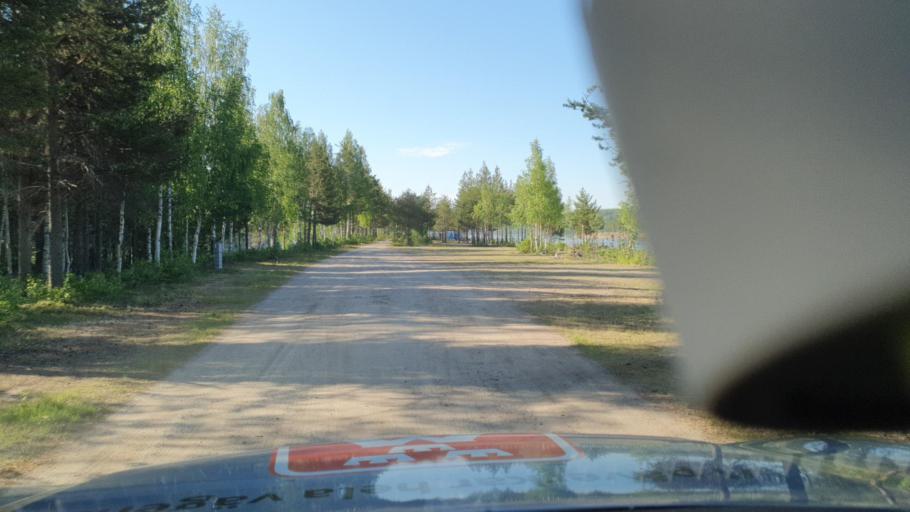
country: SE
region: Norrbotten
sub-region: Alvsbyns Kommun
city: AElvsbyn
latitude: 66.2204
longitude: 20.8595
